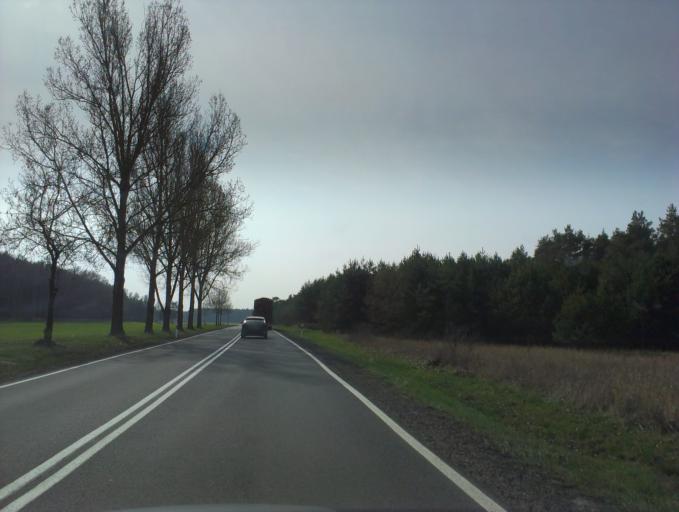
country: PL
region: Greater Poland Voivodeship
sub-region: Powiat zlotowski
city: Tarnowka
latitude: 53.2564
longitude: 16.7838
